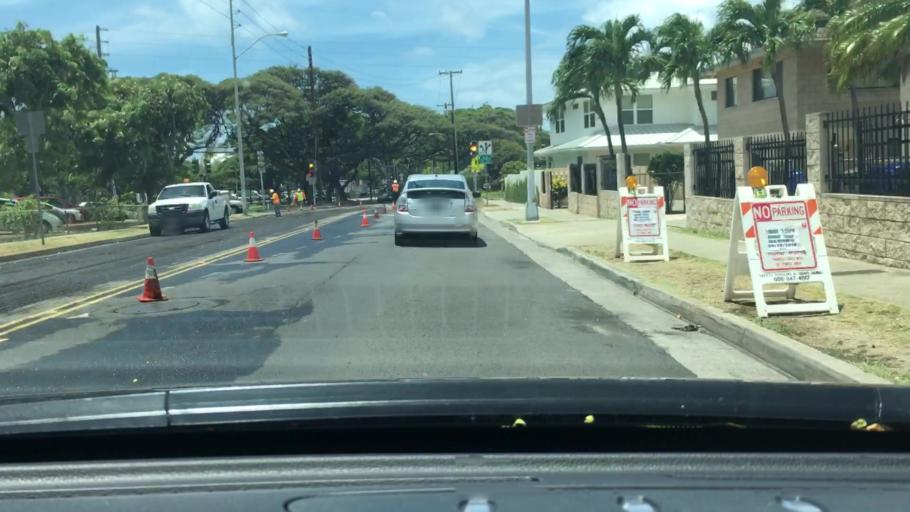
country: US
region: Hawaii
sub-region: Honolulu County
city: Honolulu
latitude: 21.2691
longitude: -157.8144
